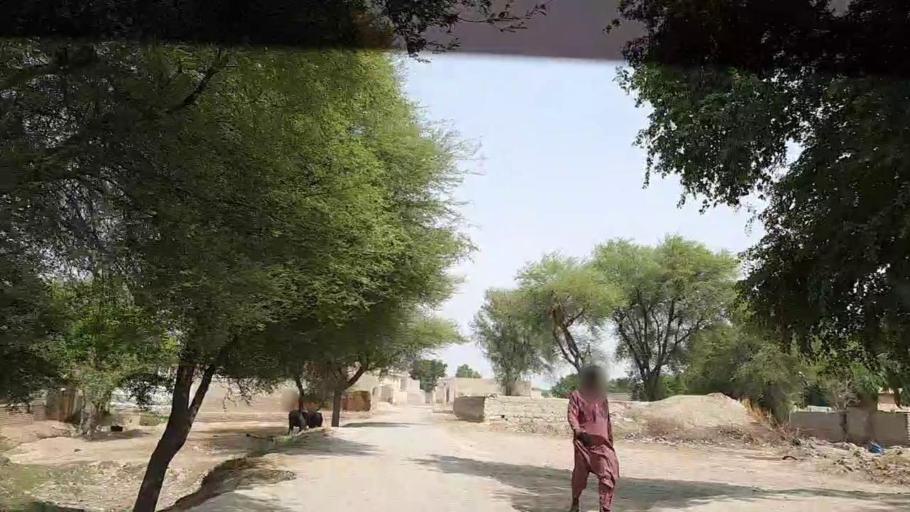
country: PK
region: Sindh
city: Khairpur Nathan Shah
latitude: 27.0777
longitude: 67.6868
